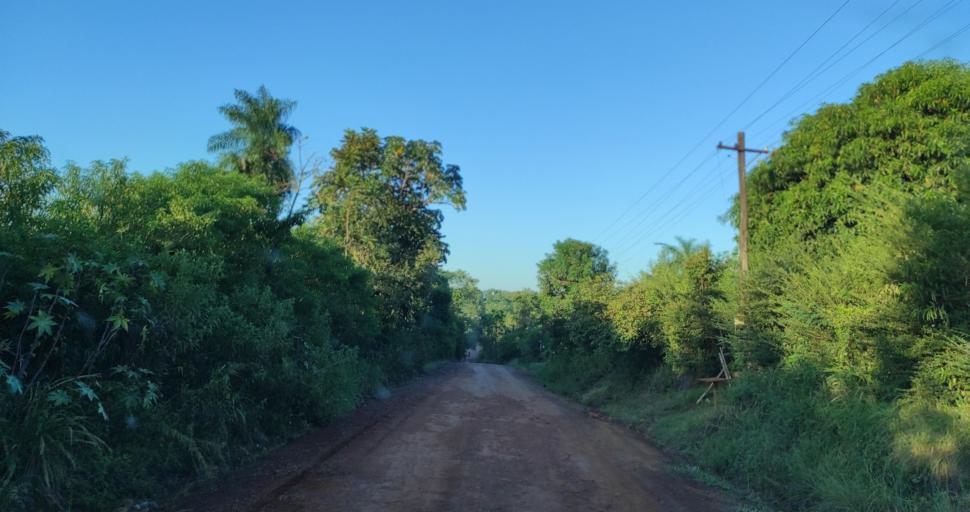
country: AR
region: Misiones
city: Gobernador Roca
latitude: -27.2232
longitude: -55.4300
